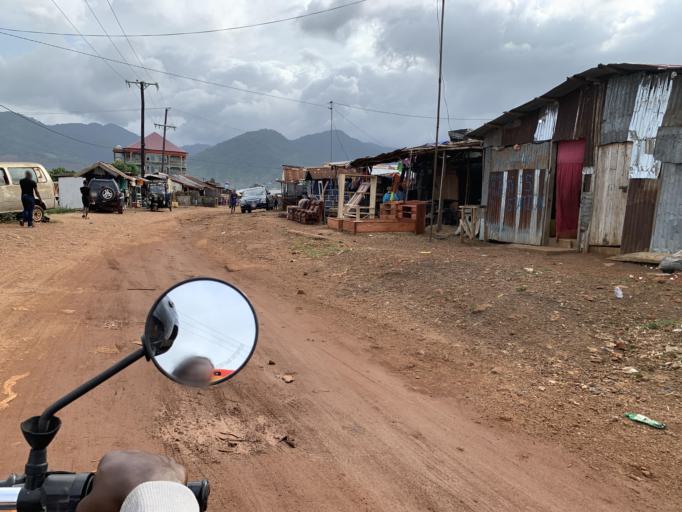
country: SL
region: Western Area
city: Hastings
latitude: 8.3901
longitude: -13.1294
